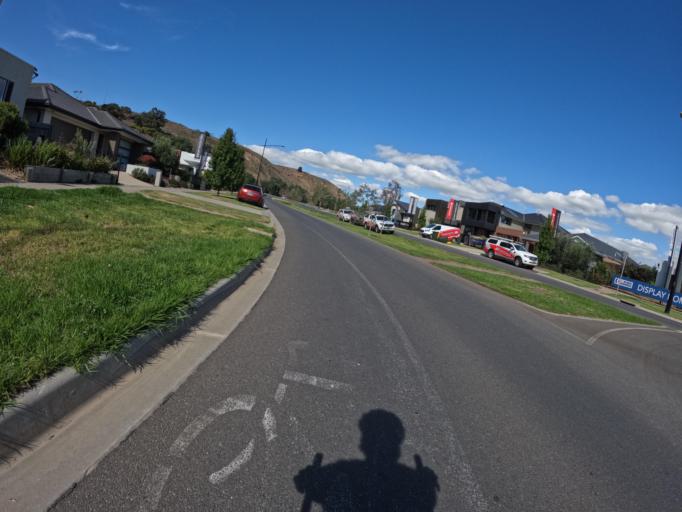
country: AU
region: Victoria
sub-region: Greater Geelong
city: Hamlyn Heights
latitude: -38.1387
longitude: 144.3130
